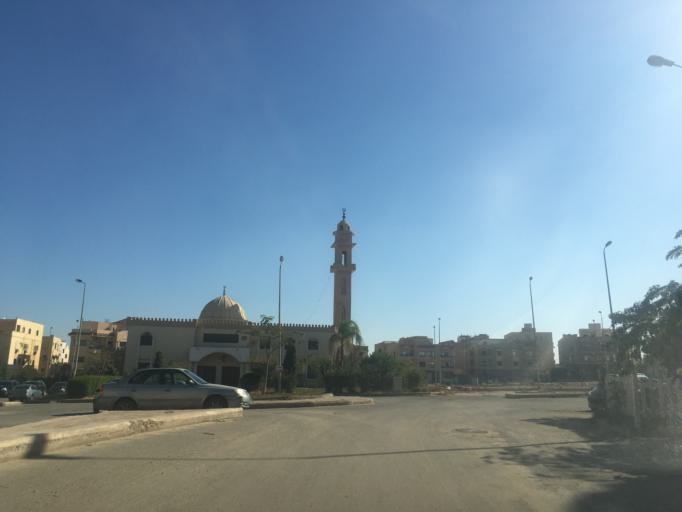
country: EG
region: Al Jizah
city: Awsim
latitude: 30.0268
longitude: 30.9838
